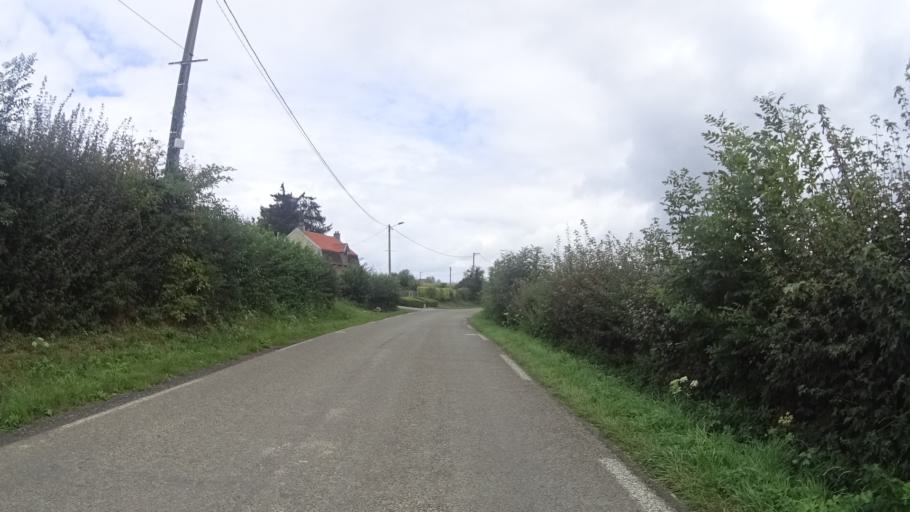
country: FR
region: Nord-Pas-de-Calais
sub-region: Departement du Nord
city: Berlaimont
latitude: 50.1856
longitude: 3.8078
